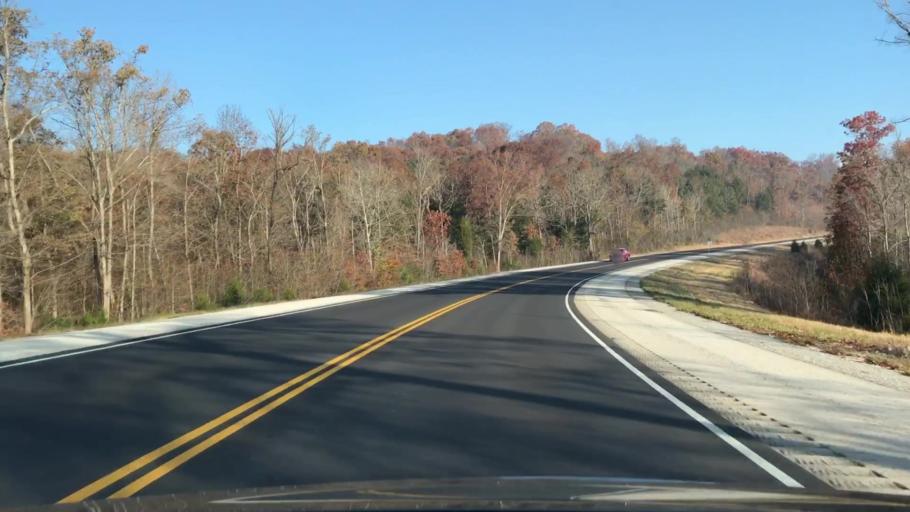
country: US
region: Kentucky
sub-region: Edmonson County
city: Brownsville
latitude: 37.0938
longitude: -86.2337
